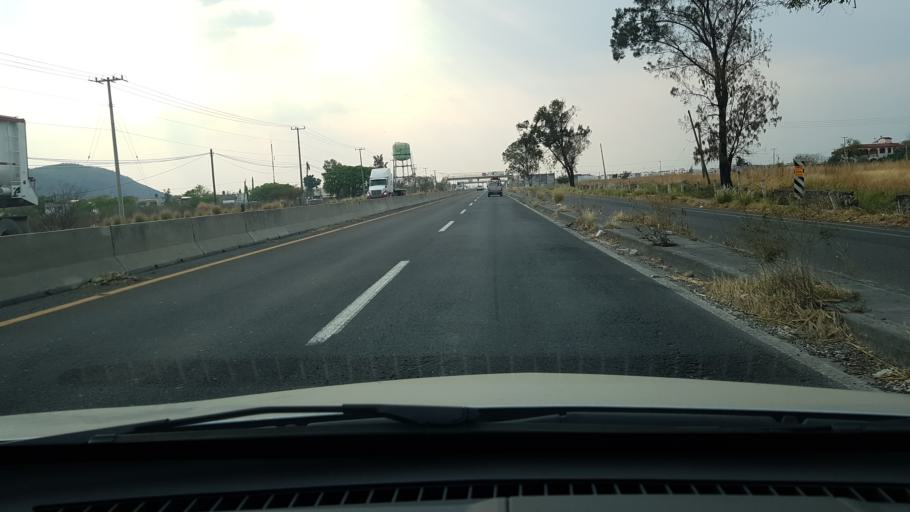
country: MX
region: Morelos
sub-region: Ayala
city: Unidad Habitacional Mariano Matamoros
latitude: 18.7492
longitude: -98.8484
